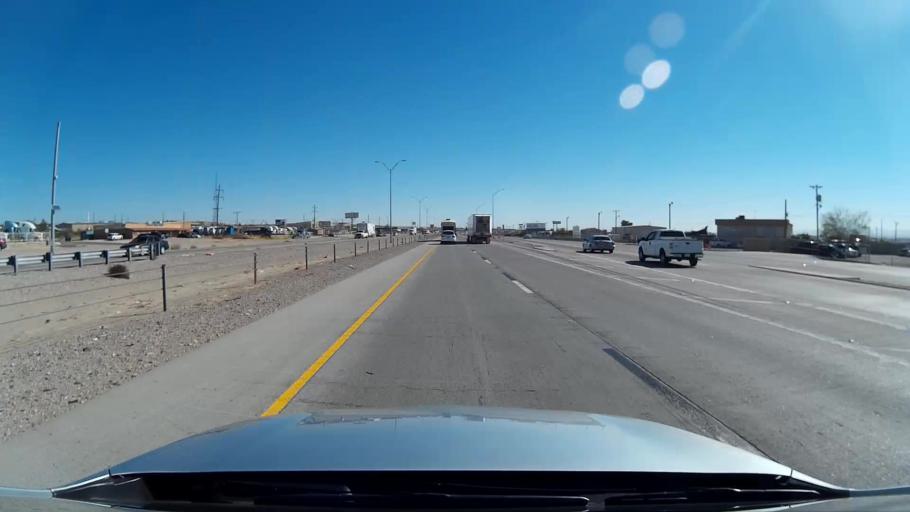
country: US
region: Texas
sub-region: El Paso County
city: Sparks
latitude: 31.6704
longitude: -106.2495
